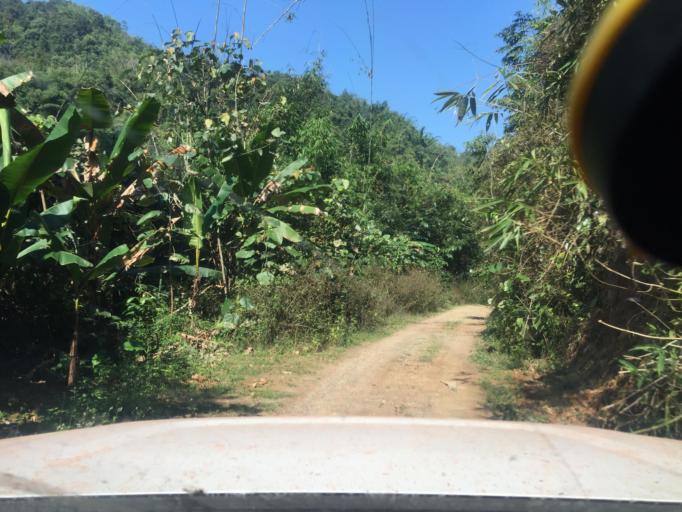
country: LA
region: Phongsali
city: Phongsali
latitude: 21.7019
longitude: 102.3940
